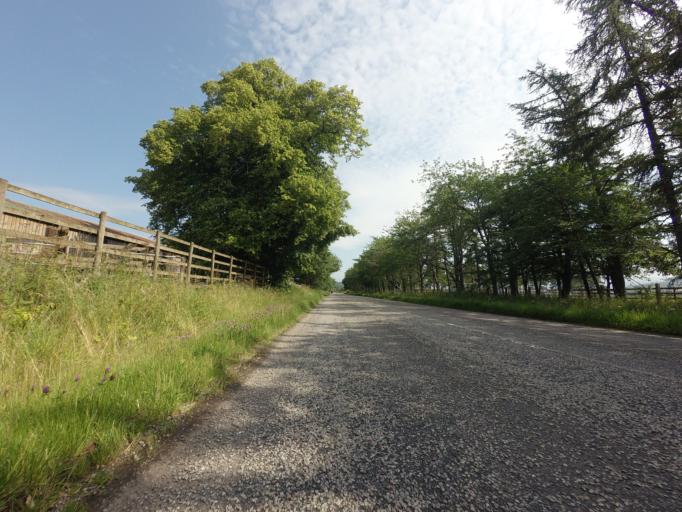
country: GB
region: Scotland
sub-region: Highland
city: Alness
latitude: 57.9149
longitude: -4.3851
